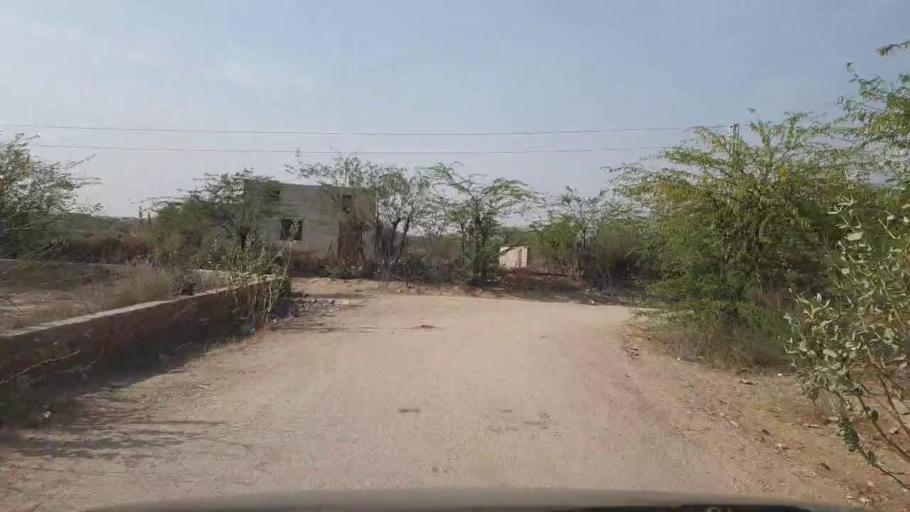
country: PK
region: Sindh
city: Umarkot
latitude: 25.3354
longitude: 69.7402
